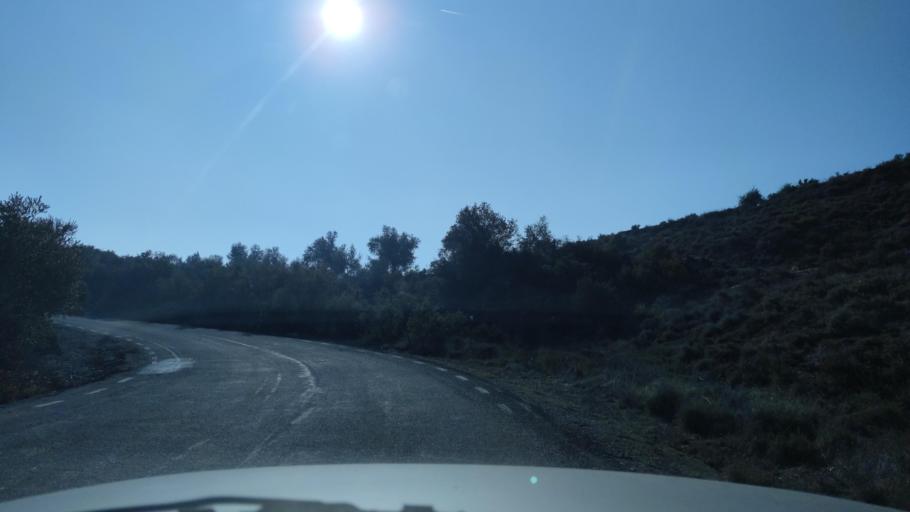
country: ES
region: Catalonia
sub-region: Provincia de Lleida
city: Torrebesses
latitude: 41.4456
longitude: 0.5583
